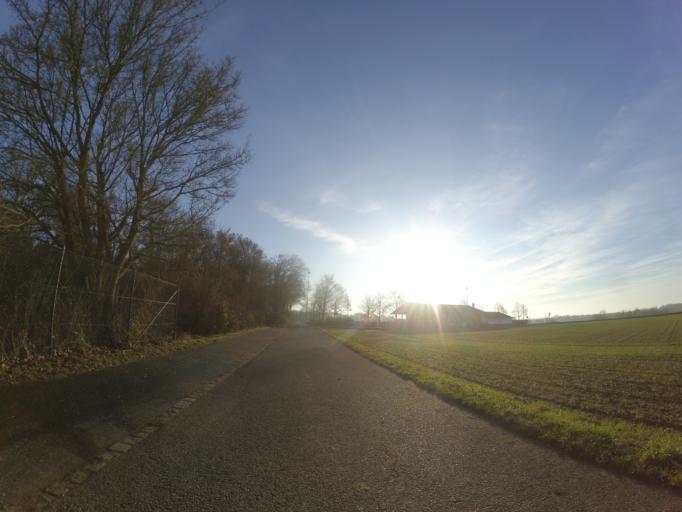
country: DE
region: Baden-Wuerttemberg
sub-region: Tuebingen Region
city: Dornstadt
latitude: 48.4372
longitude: 9.8970
